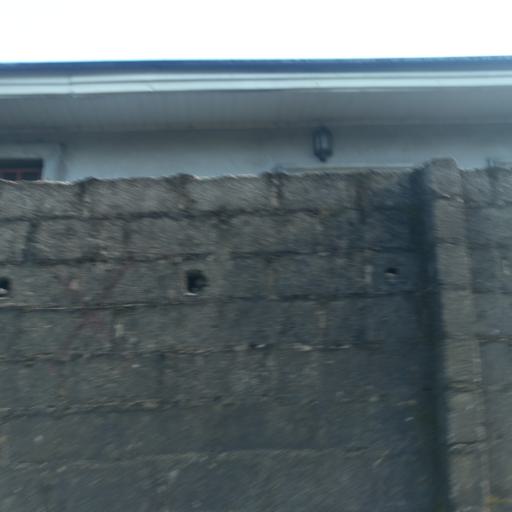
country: NG
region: Rivers
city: Port Harcourt
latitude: 4.8511
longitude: 6.9599
